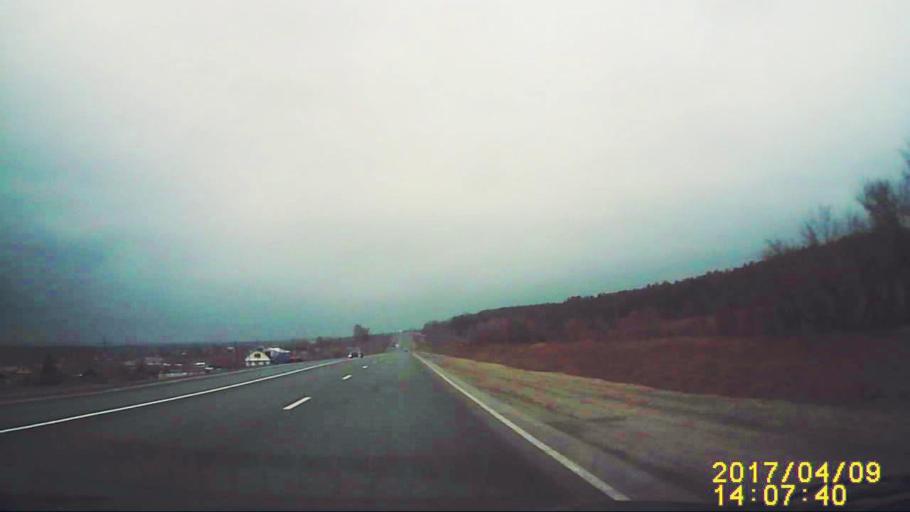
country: RU
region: Ulyanovsk
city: Silikatnyy
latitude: 54.0133
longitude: 48.2175
